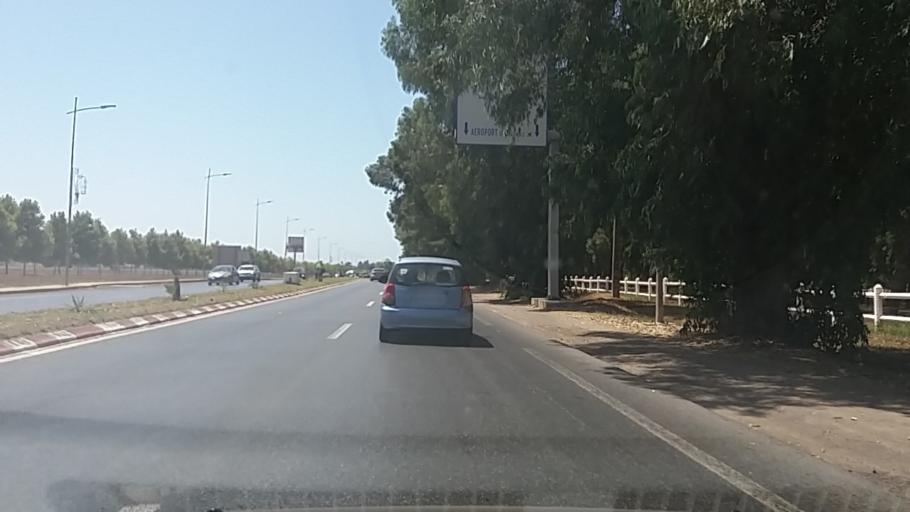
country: MA
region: Rabat-Sale-Zemmour-Zaer
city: Sale
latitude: 34.0291
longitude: -6.7350
